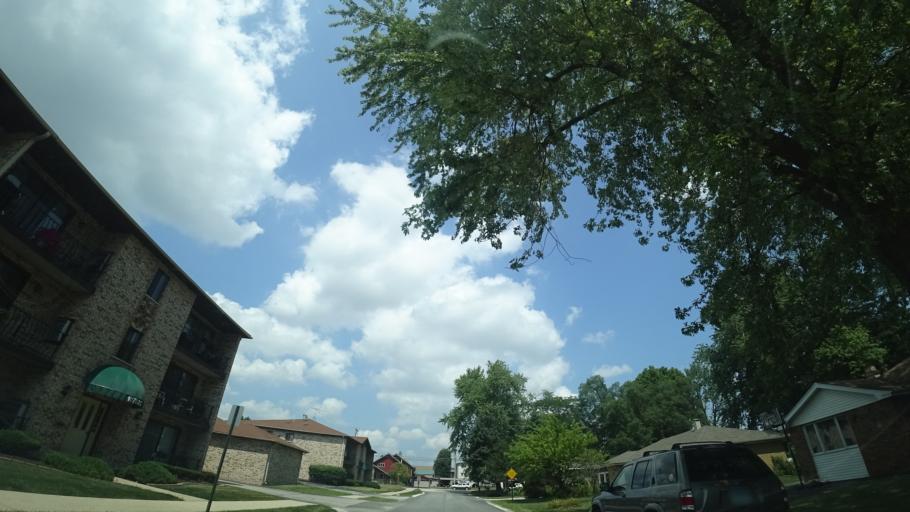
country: US
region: Illinois
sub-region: Cook County
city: Worth
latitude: 41.6964
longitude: -87.7955
